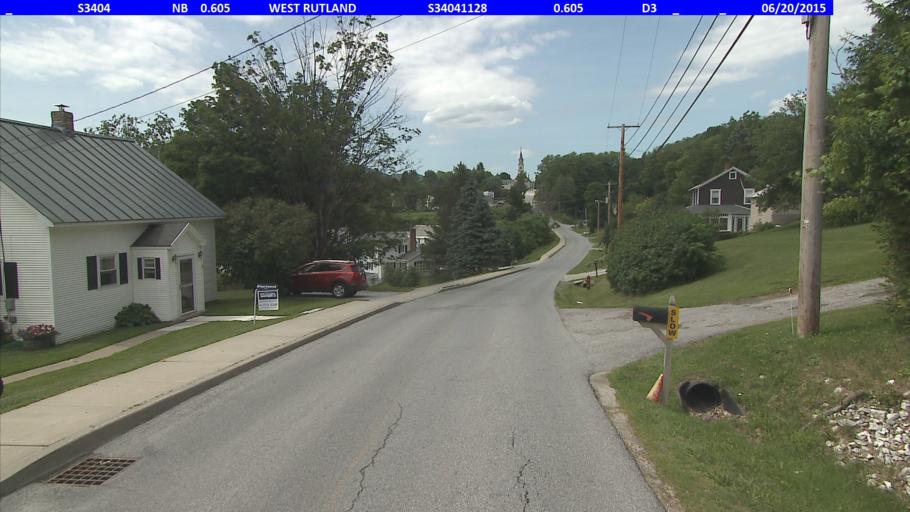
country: US
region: Vermont
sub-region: Rutland County
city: West Rutland
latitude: 43.6010
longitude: -73.0449
